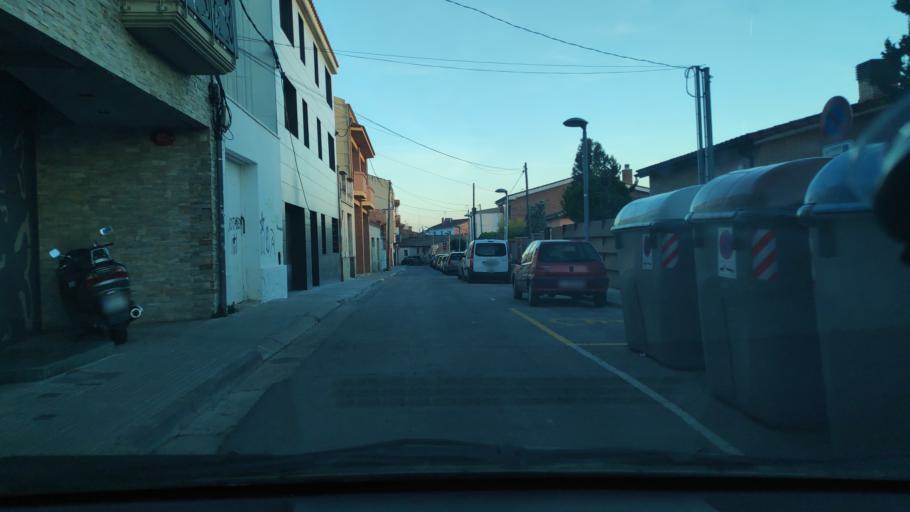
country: ES
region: Catalonia
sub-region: Provincia de Barcelona
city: Sant Quirze del Valles
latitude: 41.5333
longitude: 2.0793
